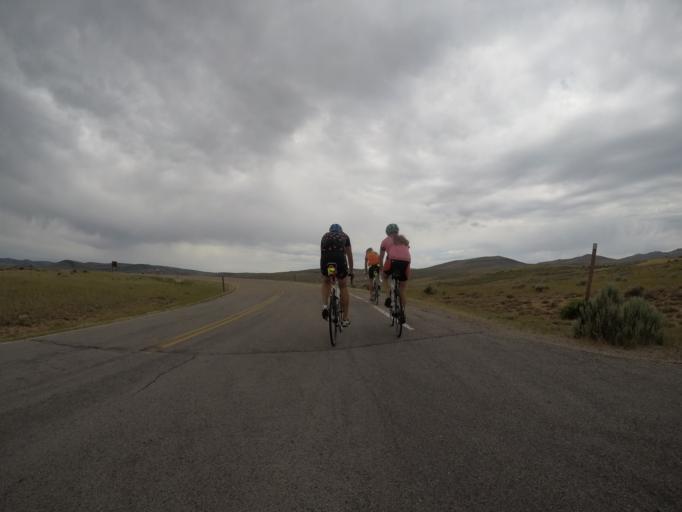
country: US
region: Wyoming
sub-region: Lincoln County
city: Kemmerer
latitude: 41.8369
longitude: -110.7727
